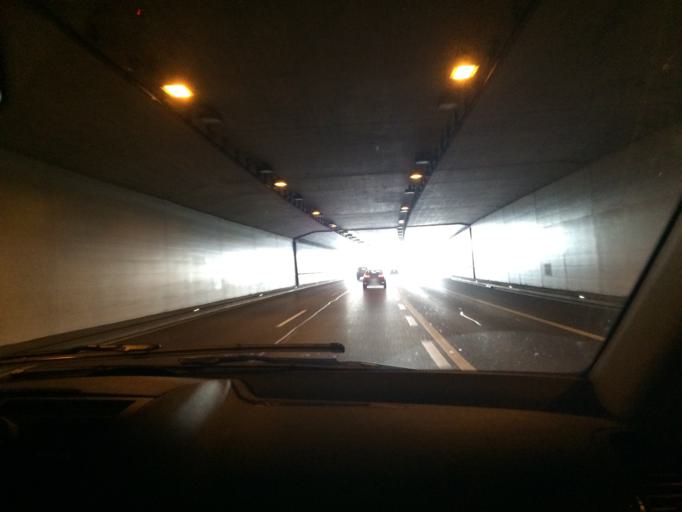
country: CH
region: Bern
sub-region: Emmental District
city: Kirchberg
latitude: 47.0858
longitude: 7.5740
